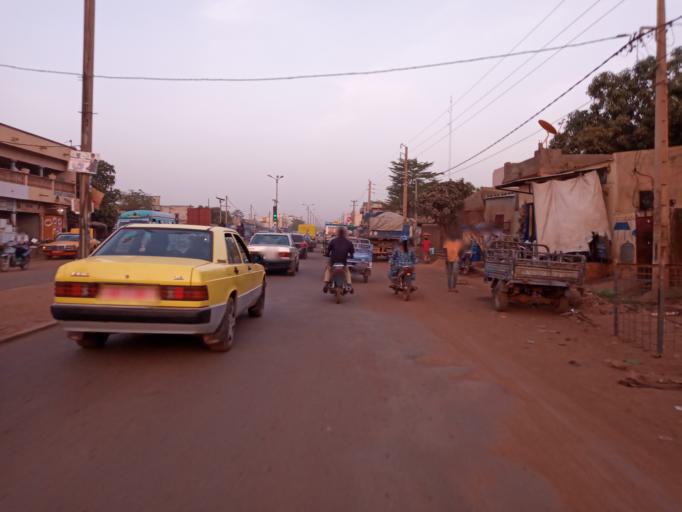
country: ML
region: Bamako
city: Bamako
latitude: 12.5730
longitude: -7.9705
